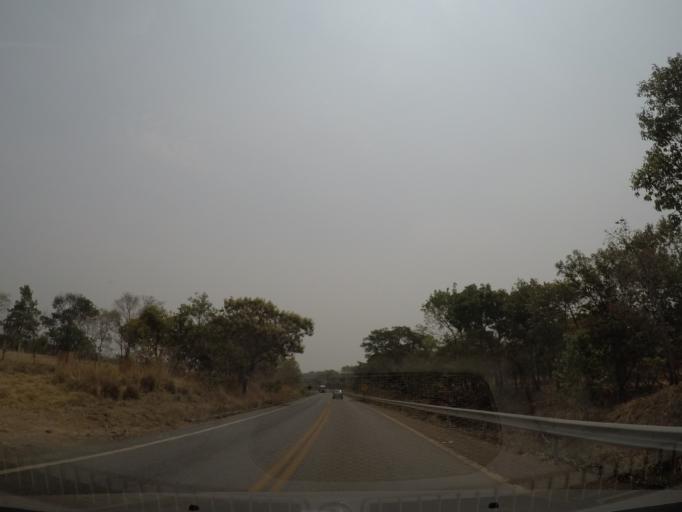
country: BR
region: Goias
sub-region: Pirenopolis
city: Pirenopolis
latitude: -15.8829
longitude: -48.9035
